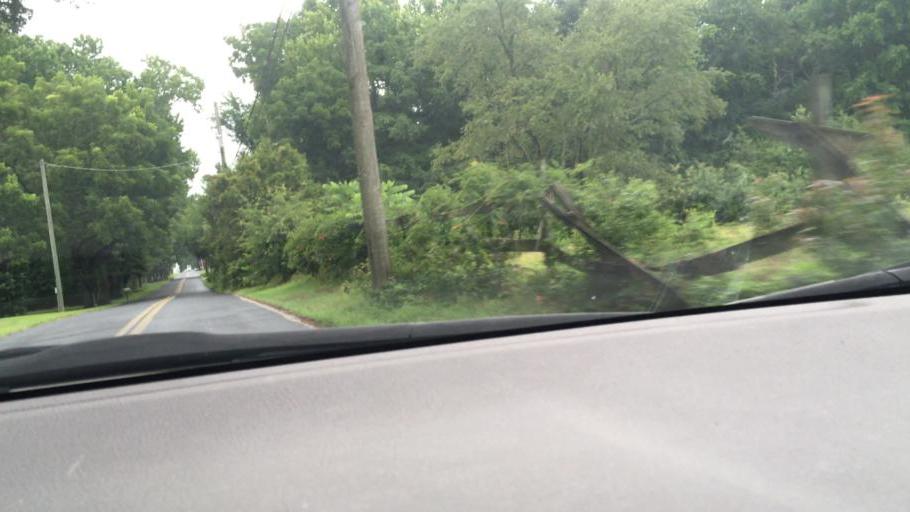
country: US
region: Maryland
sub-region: Wicomico County
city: Fruitland
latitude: 38.3388
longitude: -75.6320
